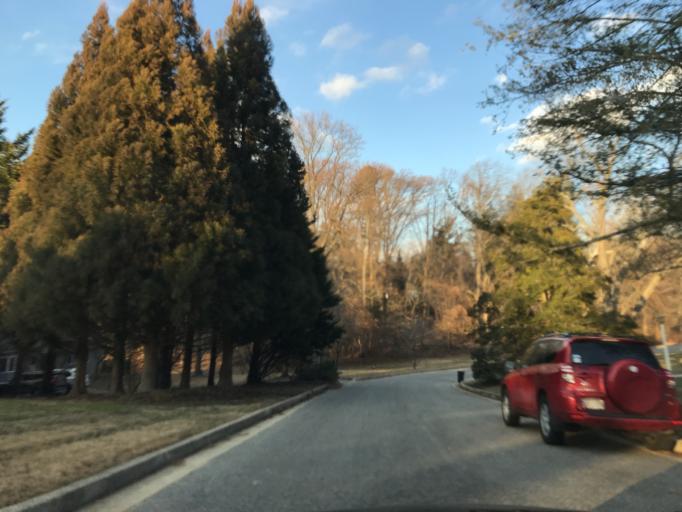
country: US
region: Maryland
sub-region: Baltimore County
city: Lutherville
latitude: 39.3987
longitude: -76.6324
